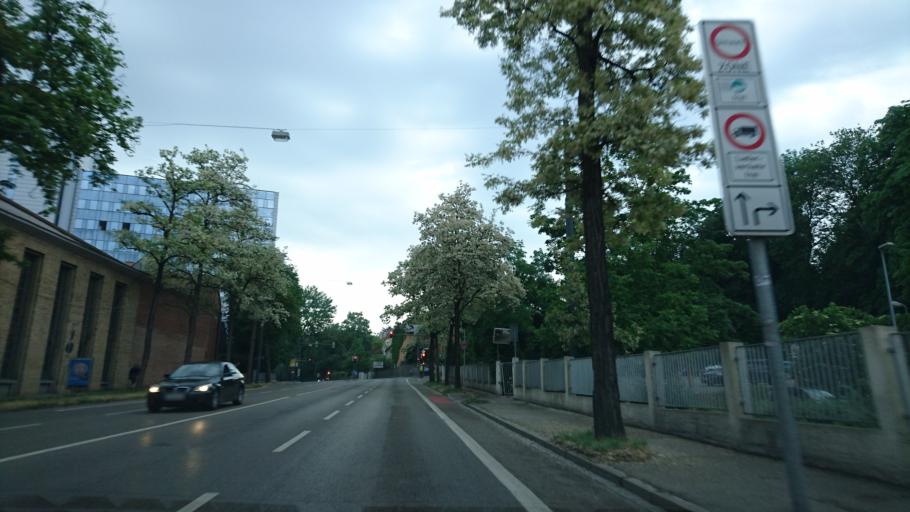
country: DE
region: Bavaria
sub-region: Swabia
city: Augsburg
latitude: 48.3803
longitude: 10.8968
